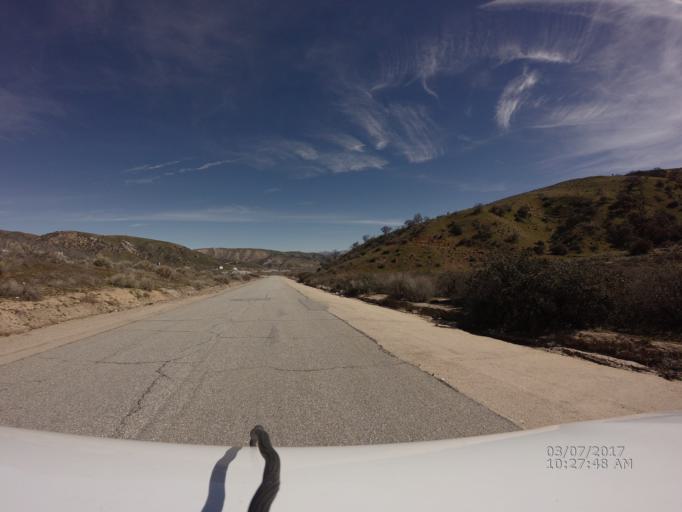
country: US
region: California
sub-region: Kern County
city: Lebec
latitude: 34.8155
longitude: -118.8828
